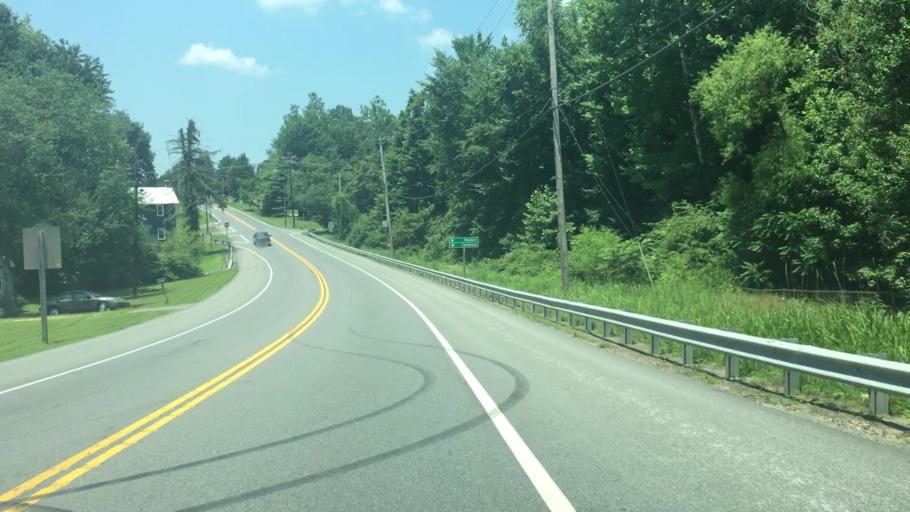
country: US
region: Maryland
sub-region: Saint Mary's County
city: Mechanicsville
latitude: 38.3747
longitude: -76.6945
